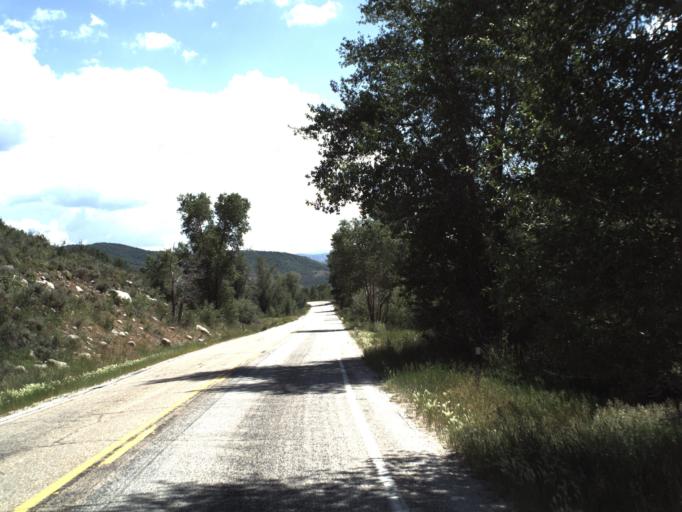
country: US
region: Utah
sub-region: Weber County
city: Wolf Creek
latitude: 41.3769
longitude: -111.5900
